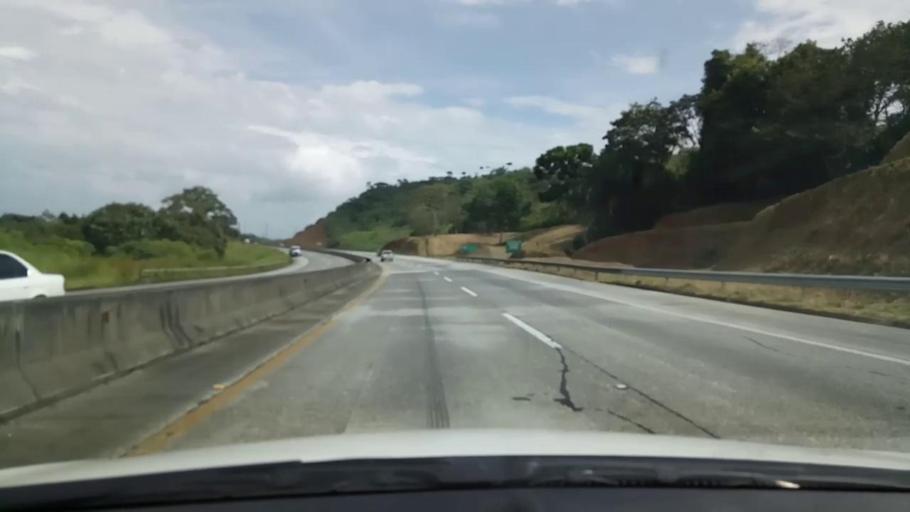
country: PA
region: Colon
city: Buena Vista
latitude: 9.2735
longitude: -79.7136
